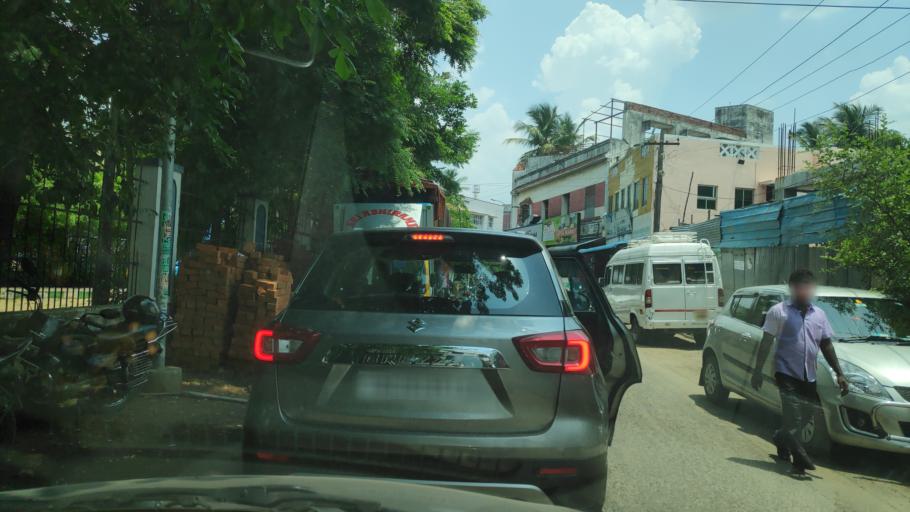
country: IN
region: Tamil Nadu
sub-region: Thiruvallur
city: Ambattur
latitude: 13.1215
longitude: 80.1495
